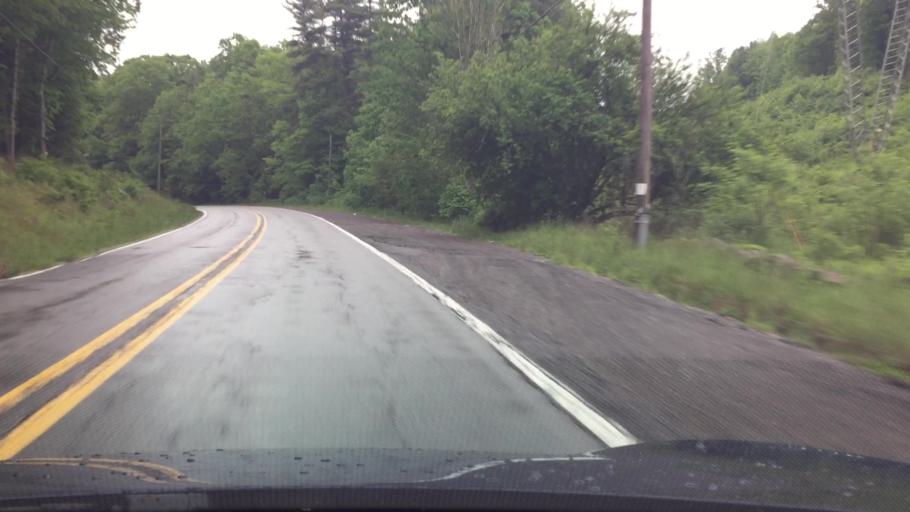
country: US
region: West Virginia
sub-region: Raleigh County
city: Shady Spring
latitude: 37.6874
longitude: -81.0587
